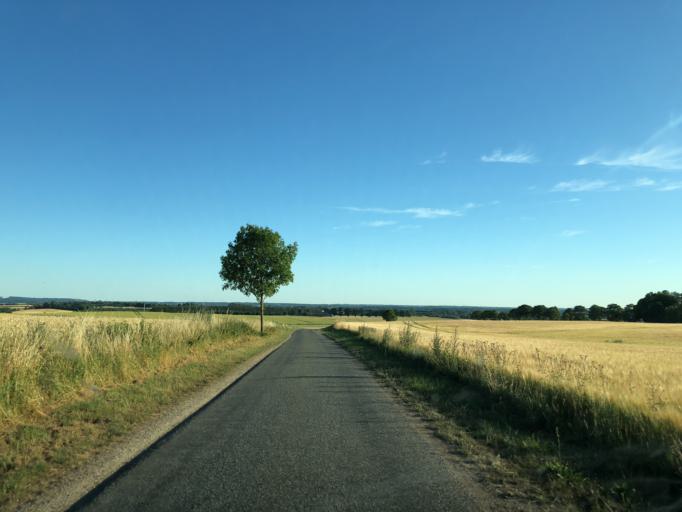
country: DK
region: Central Jutland
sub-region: Horsens Kommune
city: Horsens
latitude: 55.9093
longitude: 9.8735
